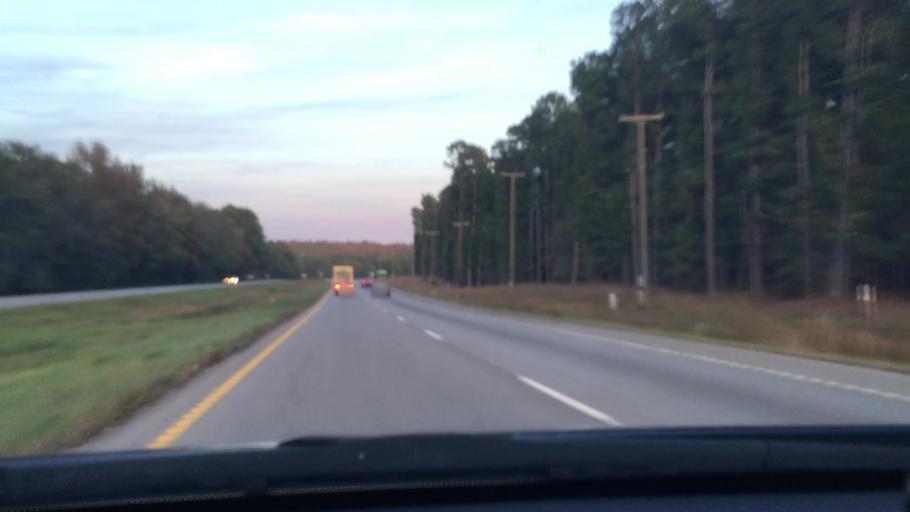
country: US
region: South Carolina
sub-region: Richland County
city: Gadsden
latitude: 33.9436
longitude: -80.7672
